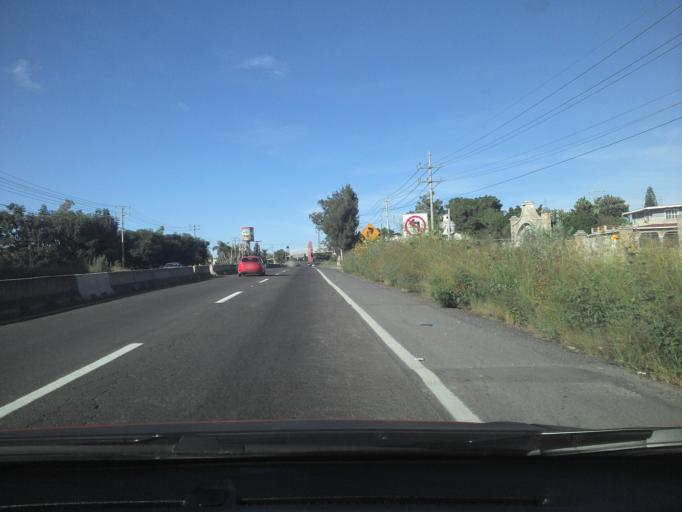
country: MX
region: Jalisco
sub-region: Tala
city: Los Ruisenores
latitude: 20.6996
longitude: -103.6890
